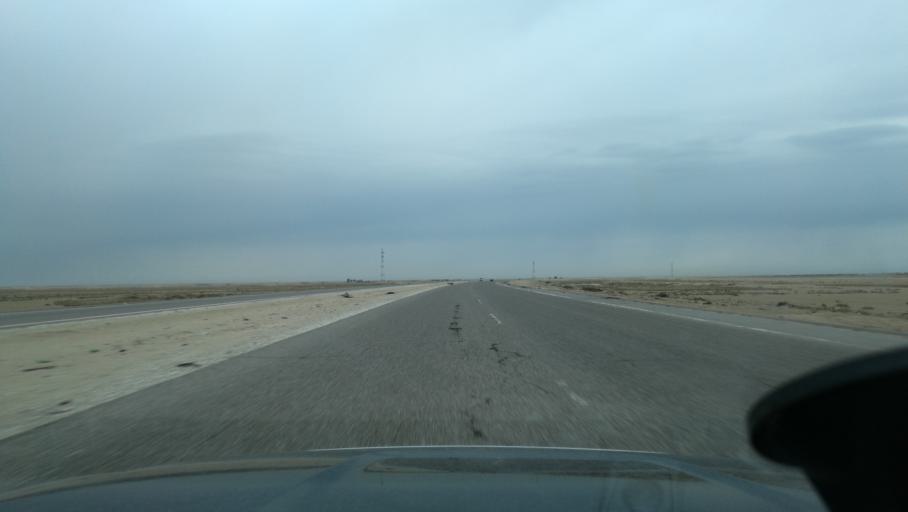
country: IQ
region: Dhi Qar
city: Suq ash Shuyukh
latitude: 30.6487
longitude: 46.6237
